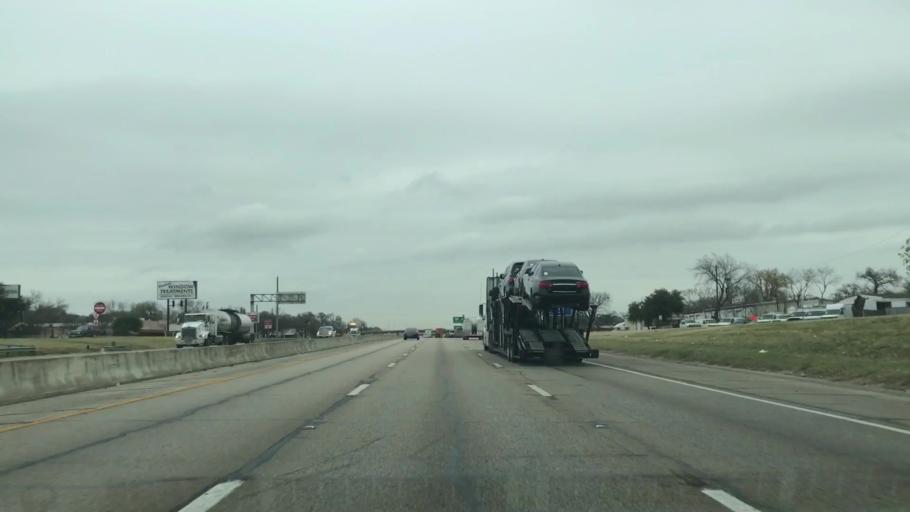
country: US
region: Texas
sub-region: Dallas County
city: Irving
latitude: 32.8016
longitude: -96.9217
